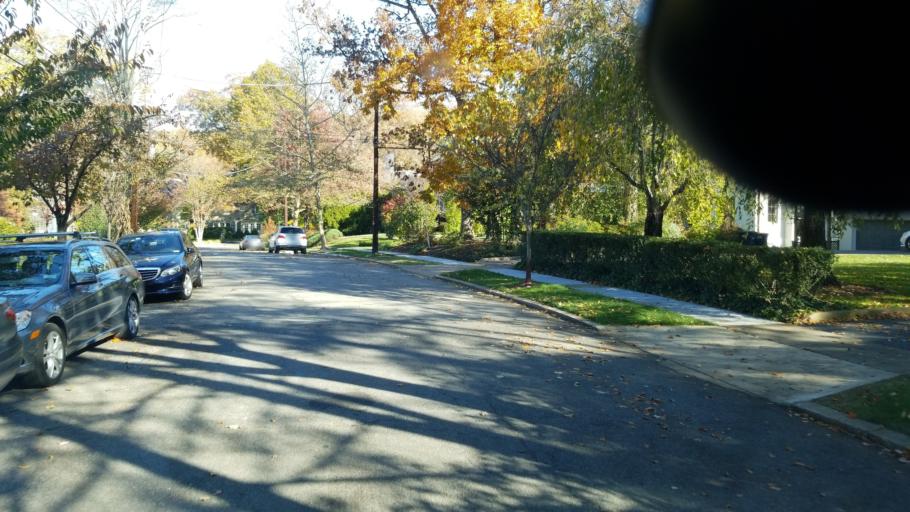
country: US
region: Maryland
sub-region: Montgomery County
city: Chevy Chase
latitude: 38.9521
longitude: -77.0564
